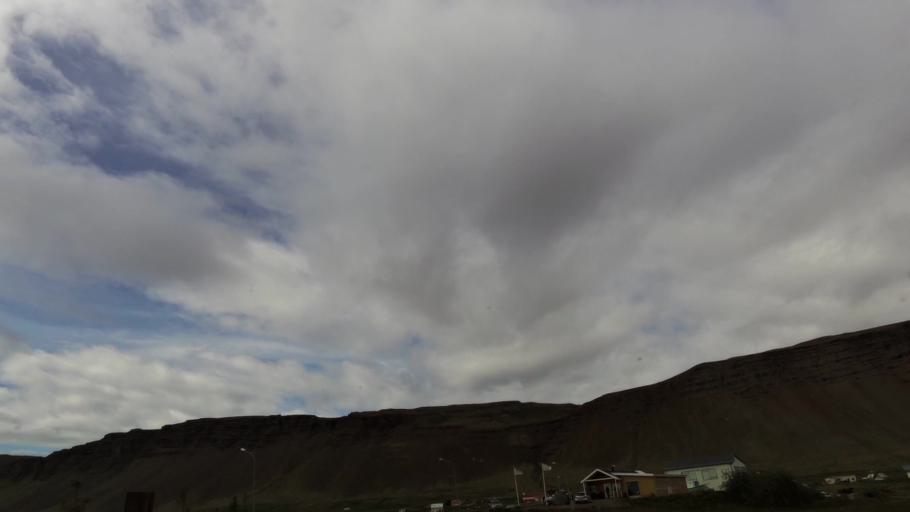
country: IS
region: West
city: Stykkisholmur
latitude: 65.4507
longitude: -22.2015
